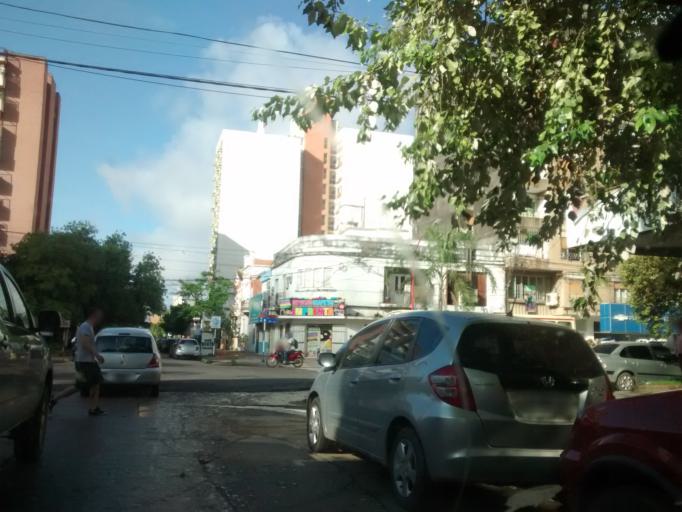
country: AR
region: Chaco
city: Resistencia
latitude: -27.4540
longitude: -58.9829
